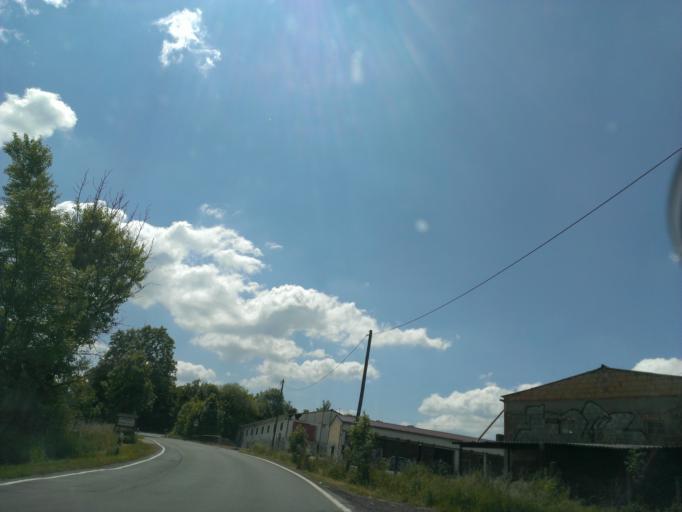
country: DE
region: Thuringia
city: Ingersleben
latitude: 50.9254
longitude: 10.9829
